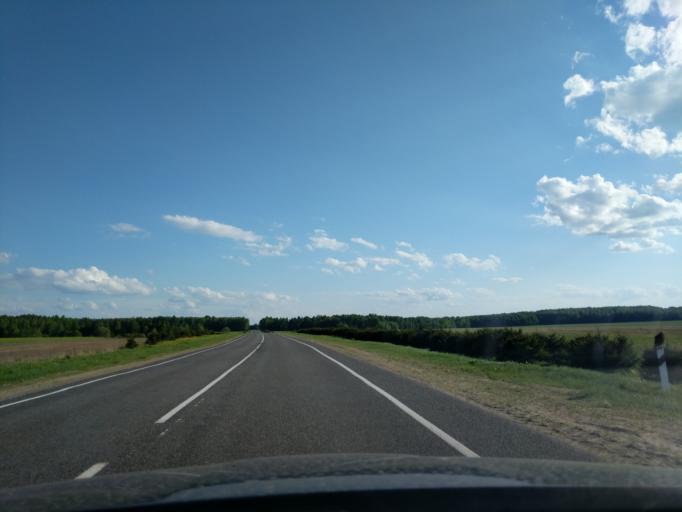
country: BY
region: Minsk
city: Kryvichy
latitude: 54.6411
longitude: 27.1702
